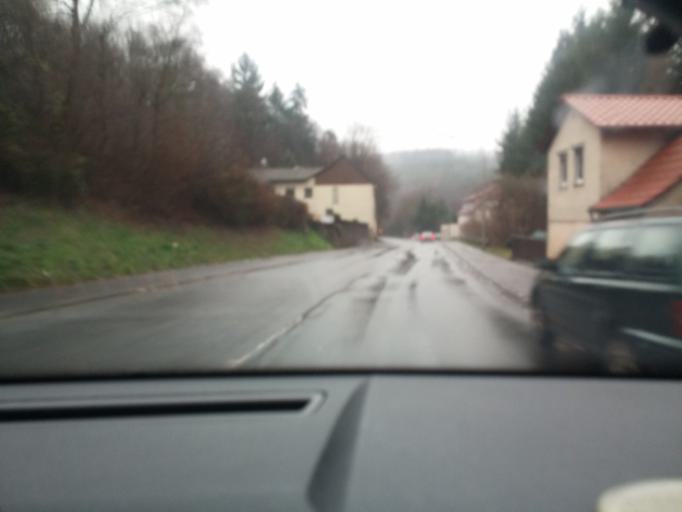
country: DE
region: Hesse
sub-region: Regierungsbezirk Darmstadt
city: Bad Konig
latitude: 49.7268
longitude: 8.9712
